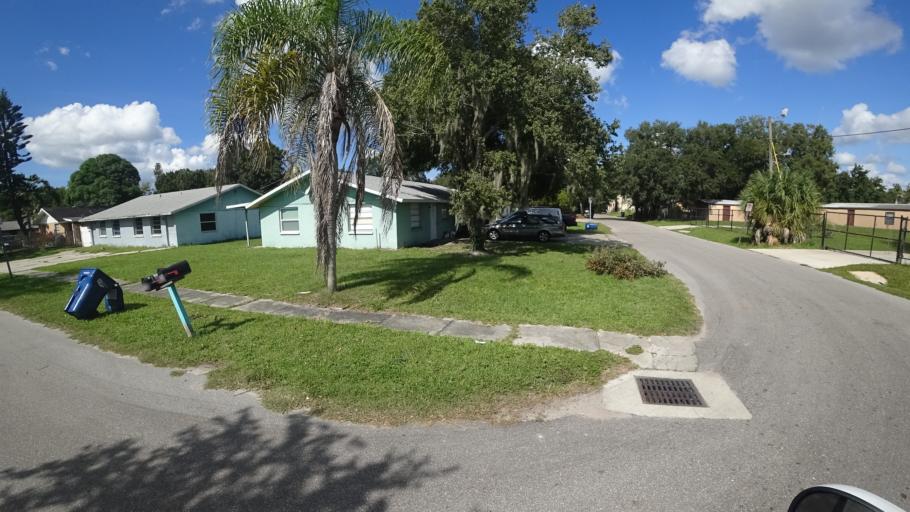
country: US
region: Florida
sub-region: Manatee County
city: West Samoset
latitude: 27.4756
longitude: -82.5666
